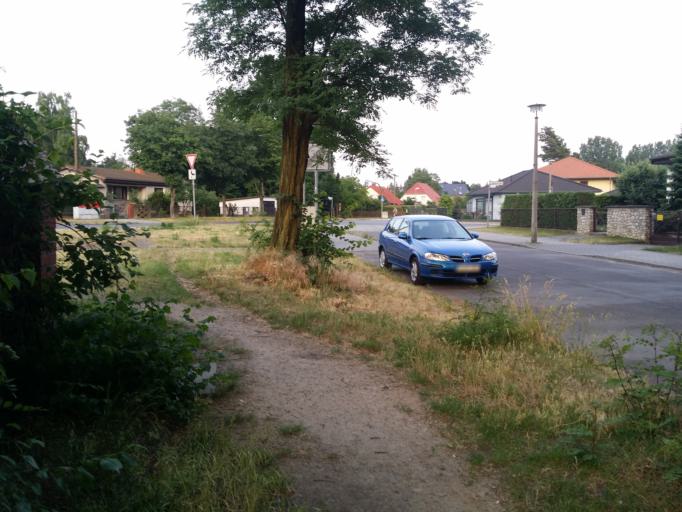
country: DE
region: Berlin
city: Altglienicke
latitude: 52.4172
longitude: 13.5386
